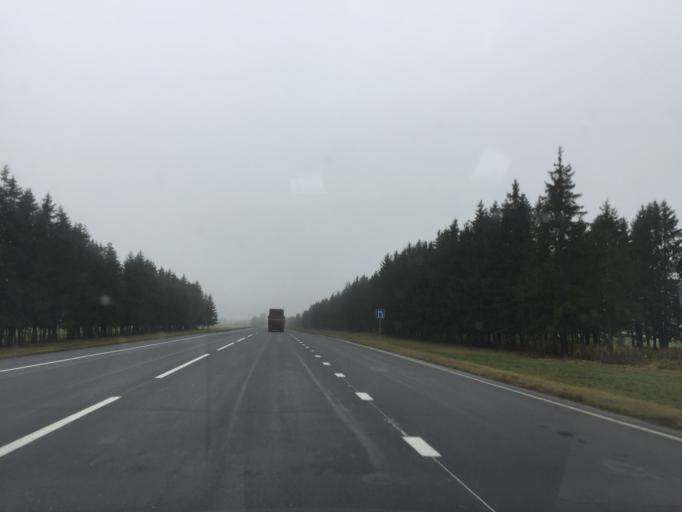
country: BY
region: Mogilev
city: Shklow
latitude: 54.2680
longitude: 30.4498
